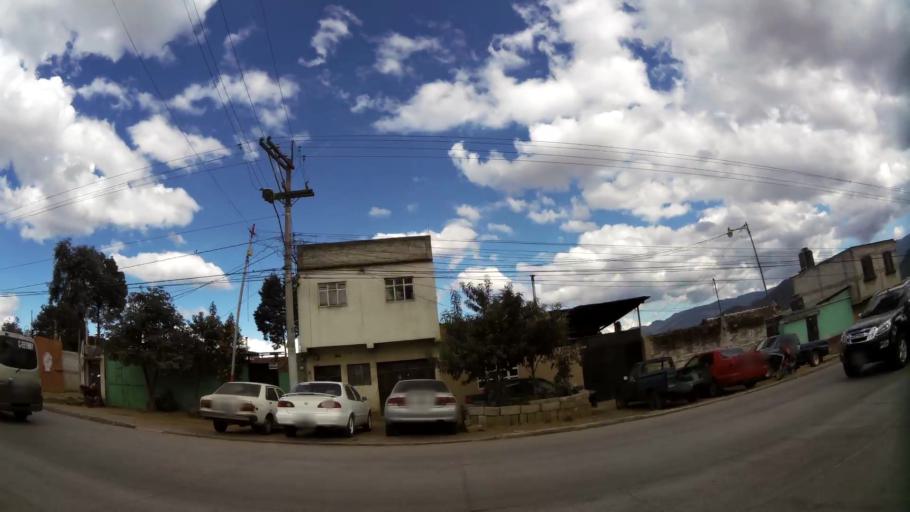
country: GT
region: Quetzaltenango
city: Quetzaltenango
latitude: 14.8425
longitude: -91.5358
